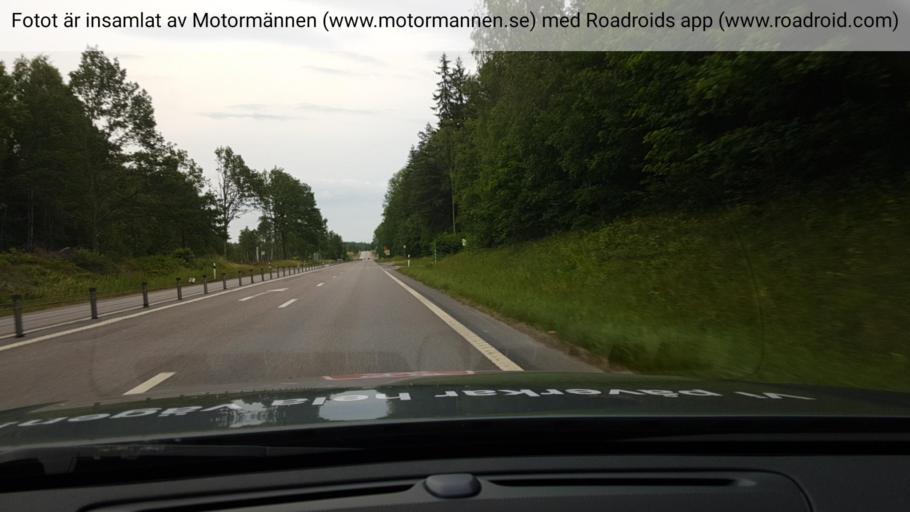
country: SE
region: OEstergoetland
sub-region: Motala Kommun
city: Motala
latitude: 58.5710
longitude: 15.0736
